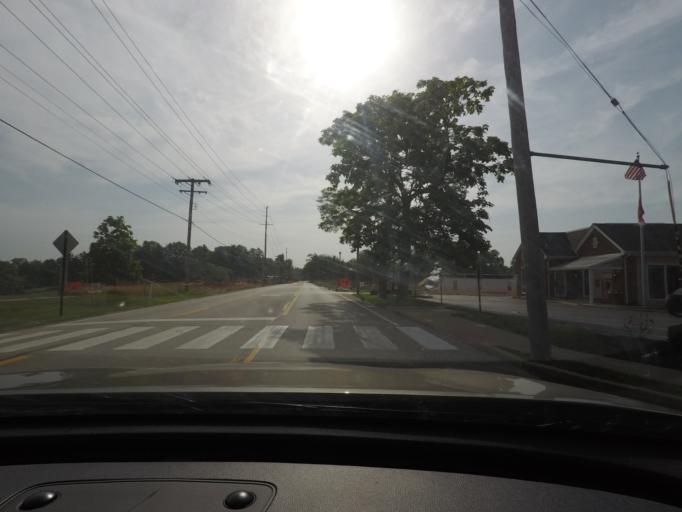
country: US
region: Missouri
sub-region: Saint Louis County
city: Town and Country
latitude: 38.6272
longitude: -90.4811
